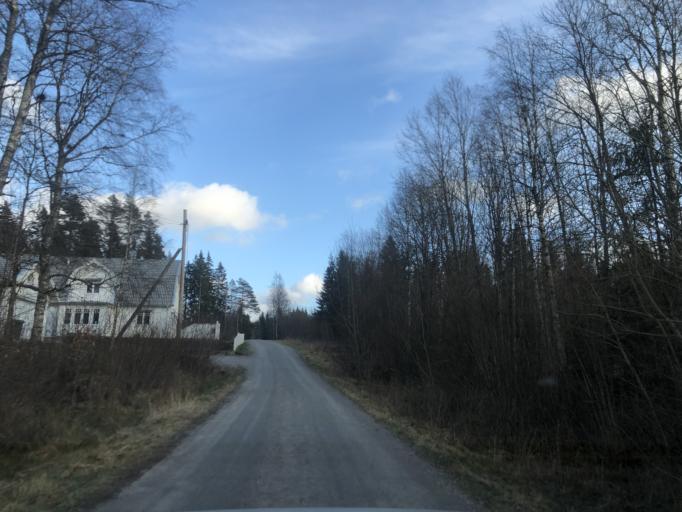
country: SE
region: Vaestra Goetaland
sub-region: Ulricehamns Kommun
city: Ulricehamn
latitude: 57.7787
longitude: 13.4310
